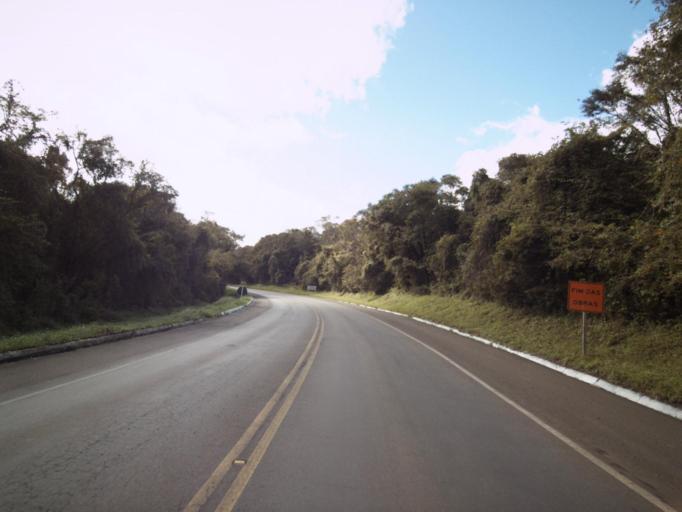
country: BR
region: Santa Catarina
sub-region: Concordia
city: Concordia
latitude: -27.1798
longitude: -51.9154
